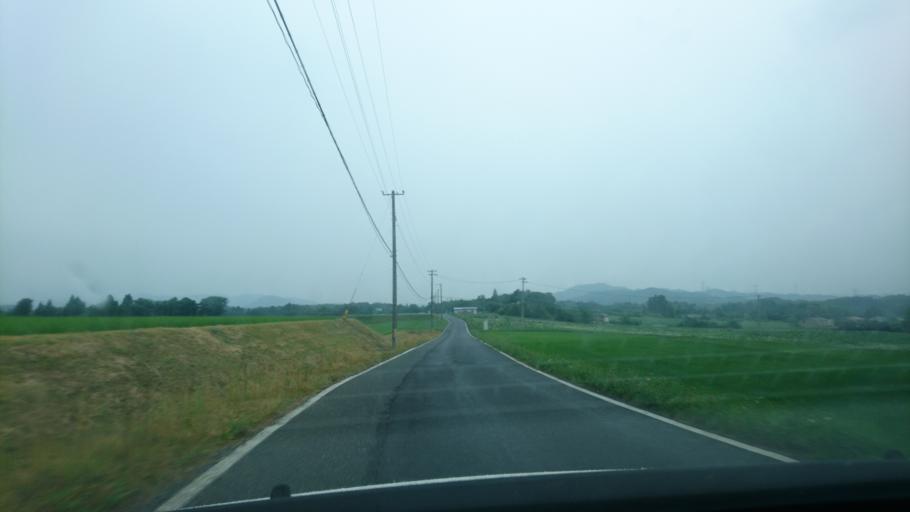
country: JP
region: Iwate
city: Ichinoseki
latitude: 38.9038
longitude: 141.1965
